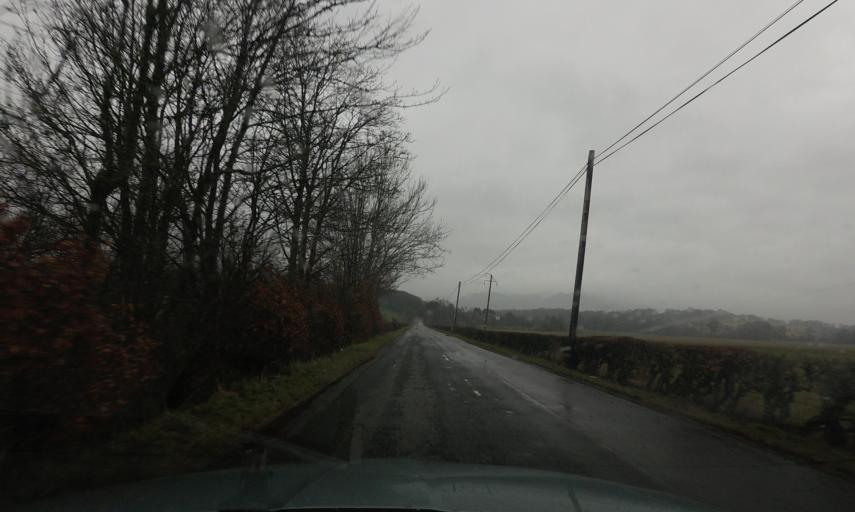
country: GB
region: Scotland
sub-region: Stirling
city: Balfron
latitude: 56.1496
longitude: -4.3608
